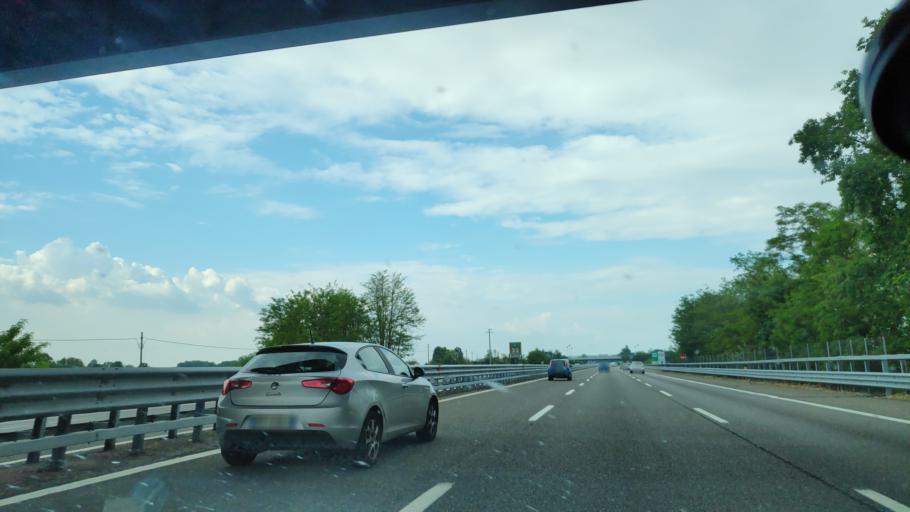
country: IT
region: Lombardy
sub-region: Provincia di Pavia
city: Pieve Albignola
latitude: 45.1376
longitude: 8.9850
